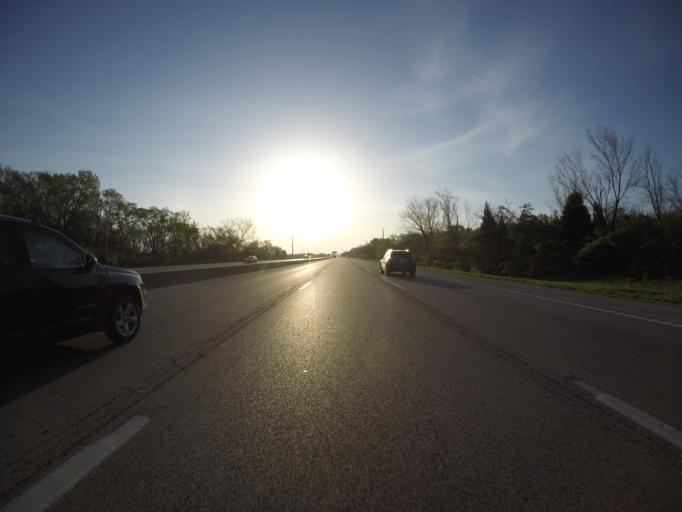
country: US
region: Missouri
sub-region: Jackson County
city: Grandview
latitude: 38.9383
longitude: -94.4967
